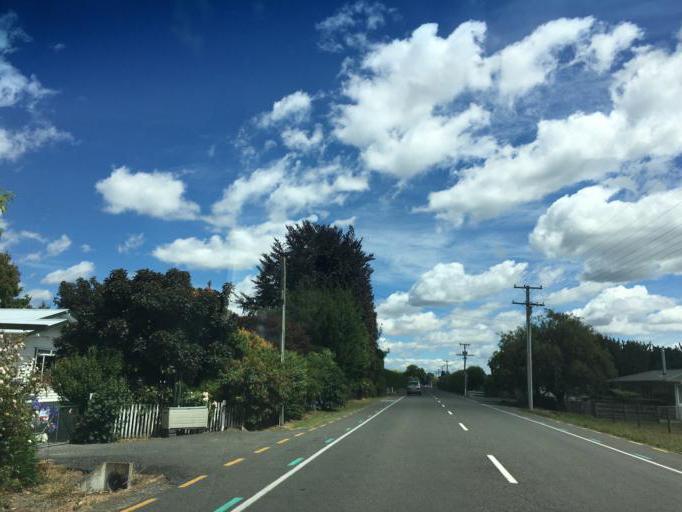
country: NZ
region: Hawke's Bay
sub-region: Hastings District
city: Hastings
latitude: -39.6549
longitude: 176.8707
